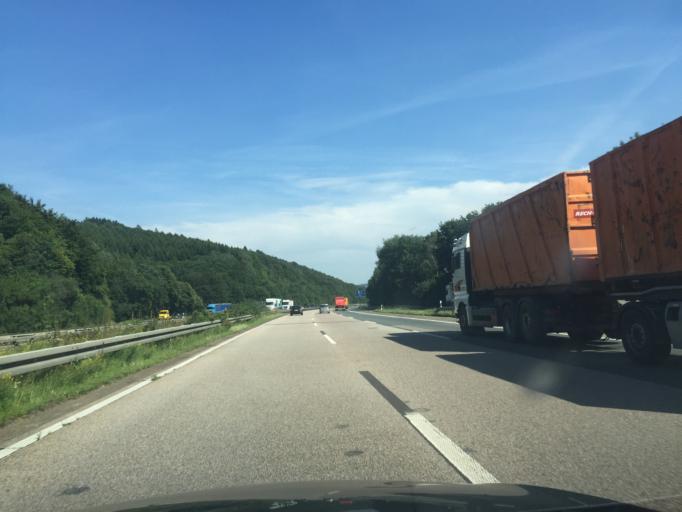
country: DE
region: North Rhine-Westphalia
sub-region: Regierungsbezirk Arnsberg
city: Neunkirchen
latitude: 50.8358
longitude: 8.0143
